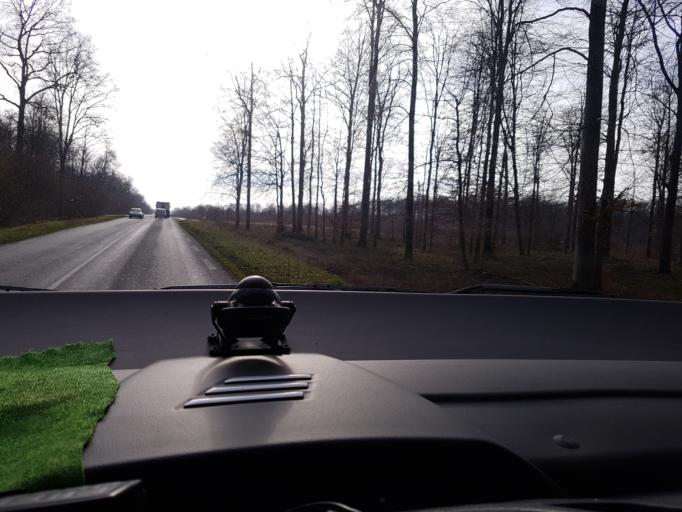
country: FR
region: Nord-Pas-de-Calais
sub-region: Departement du Nord
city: Fourmies
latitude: 49.9935
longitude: 4.0362
